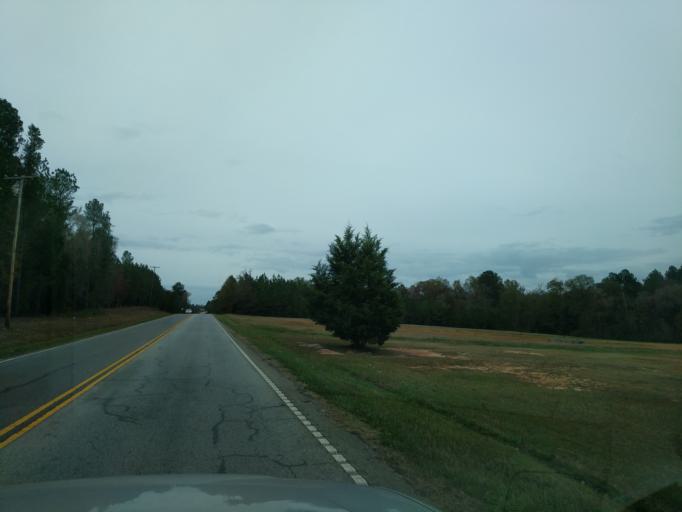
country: US
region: South Carolina
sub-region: Saluda County
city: Saluda
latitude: 34.0274
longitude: -81.7687
